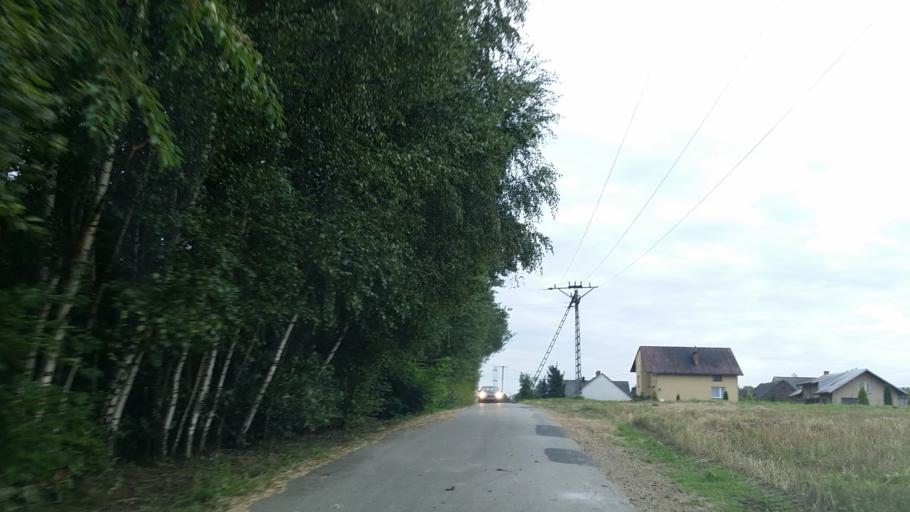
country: PL
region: Lesser Poland Voivodeship
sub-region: Powiat wadowicki
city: Spytkowice
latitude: 49.9884
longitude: 19.4990
